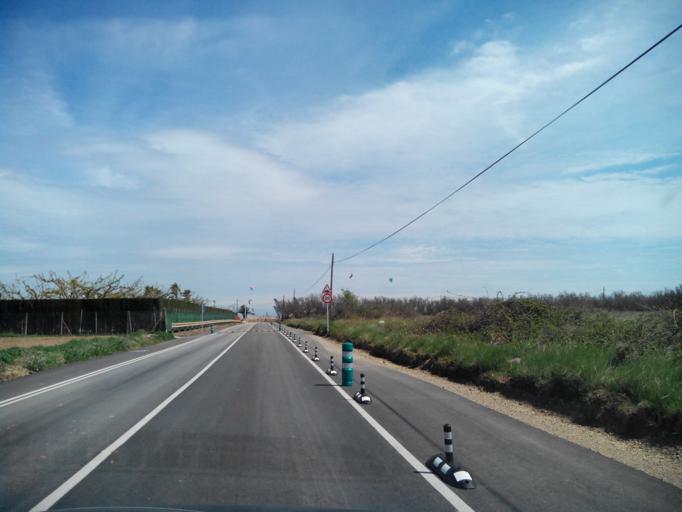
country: ES
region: Catalonia
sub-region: Provincia de Girona
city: Sant Pere Pescador
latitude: 42.1885
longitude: 3.1056
